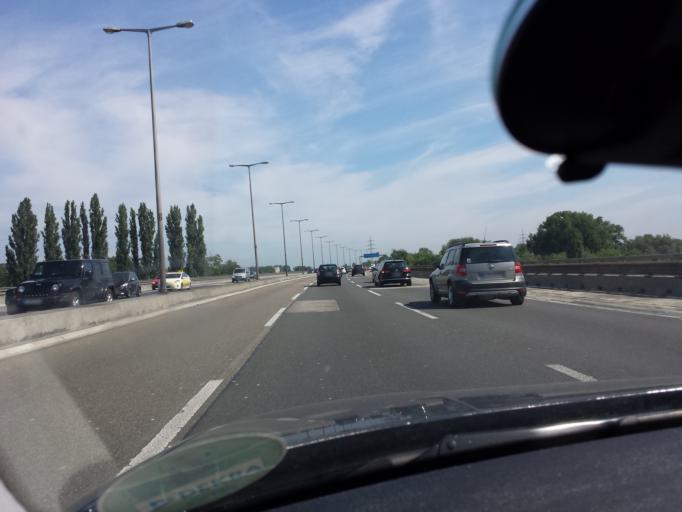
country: DE
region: Berlin
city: Charlottenburg Bezirk
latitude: 52.5271
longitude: 13.2821
